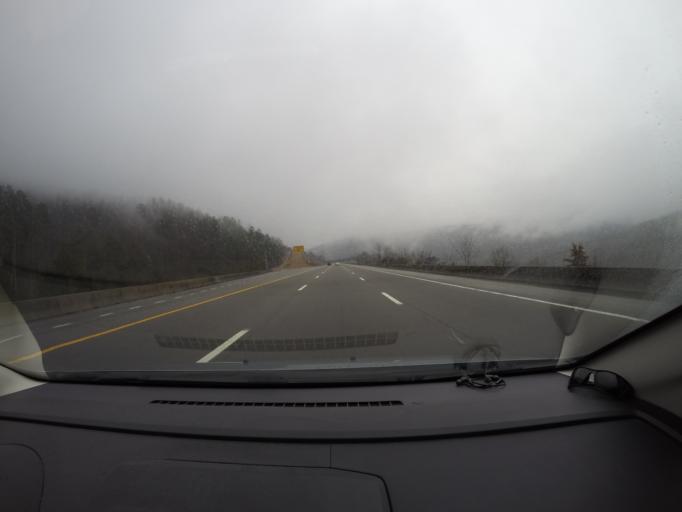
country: US
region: Tennessee
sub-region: Marion County
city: Monteagle
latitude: 35.1835
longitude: -85.8119
